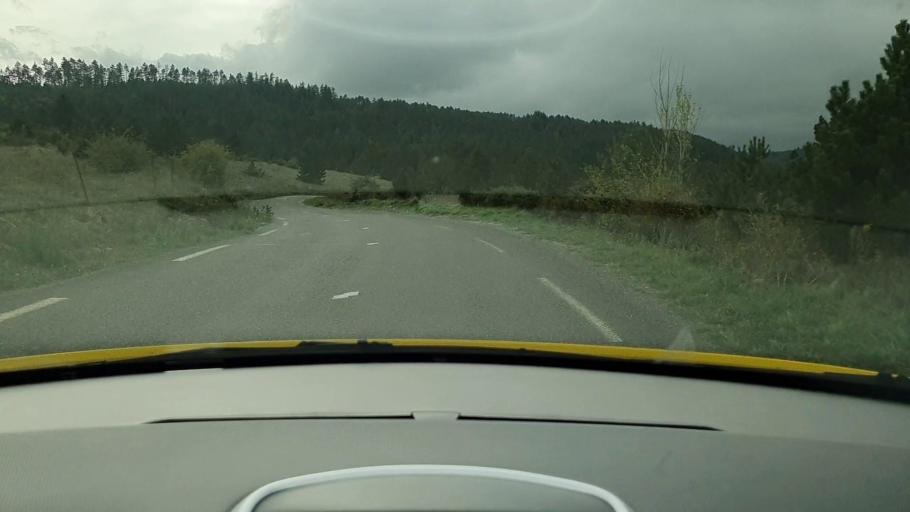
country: FR
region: Languedoc-Roussillon
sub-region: Departement de la Lozere
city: Meyrueis
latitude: 44.0929
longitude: 3.3715
